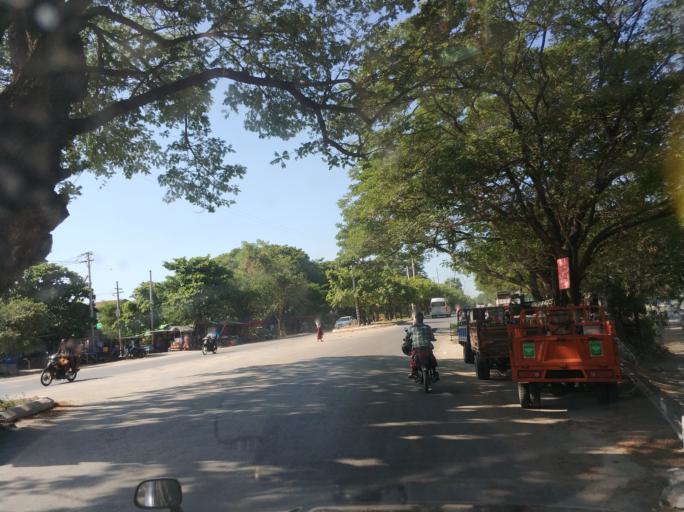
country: MM
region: Mandalay
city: Mandalay
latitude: 21.9687
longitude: 96.0563
